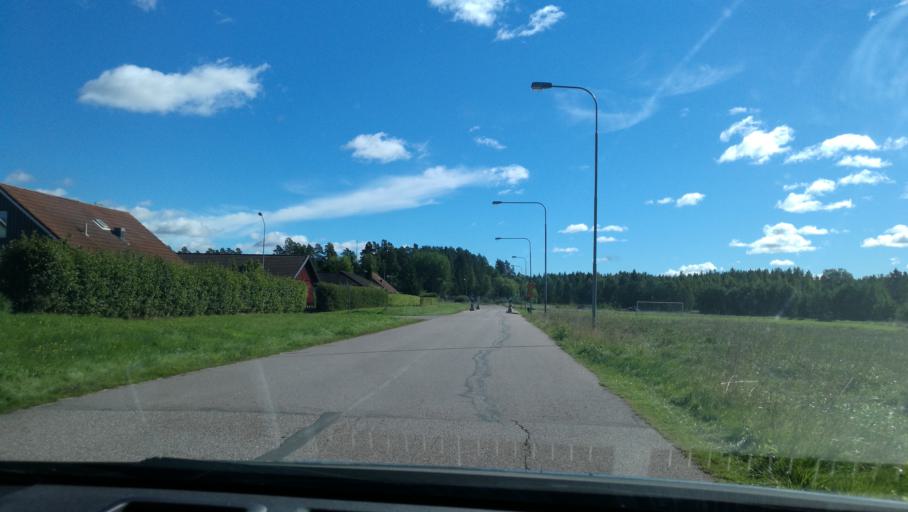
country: SE
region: Vaestmanland
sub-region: Surahammars Kommun
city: Surahammar
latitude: 59.6908
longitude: 16.2370
